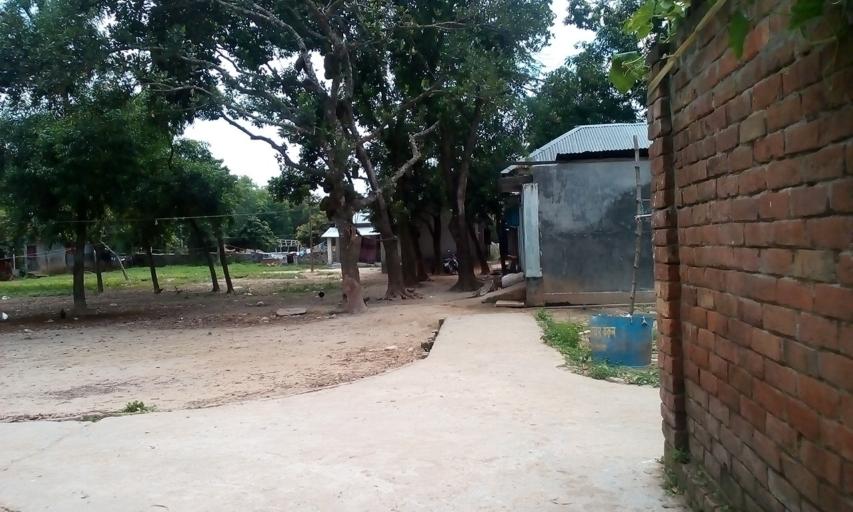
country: BD
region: Rangpur Division
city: Parbatipur
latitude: 25.4016
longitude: 88.9910
